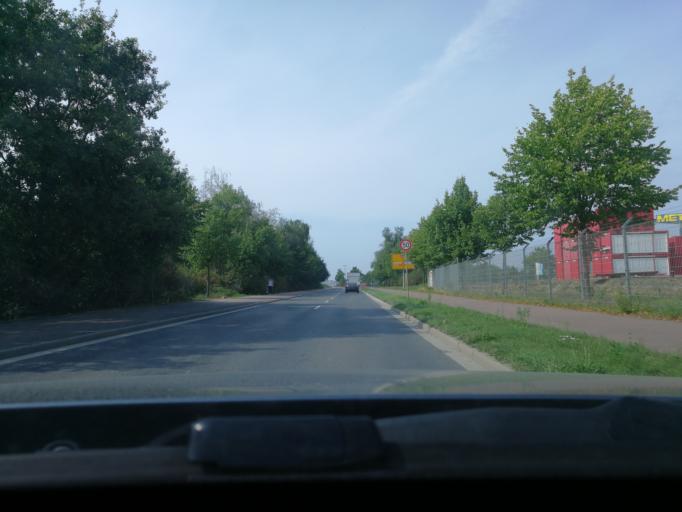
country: DE
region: North Rhine-Westphalia
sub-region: Regierungsbezirk Dusseldorf
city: Dusseldorf
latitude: 51.1616
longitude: 6.7546
